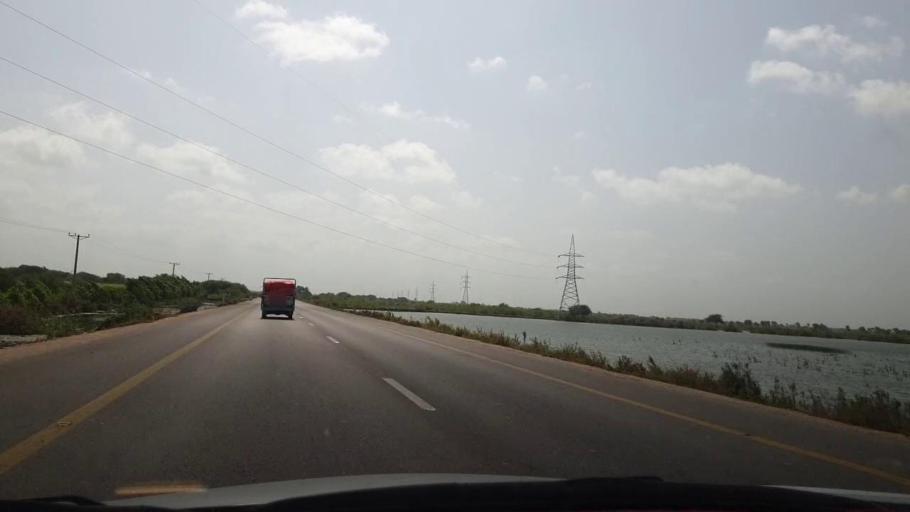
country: PK
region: Sindh
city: Talhar
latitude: 24.9246
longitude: 68.7193
